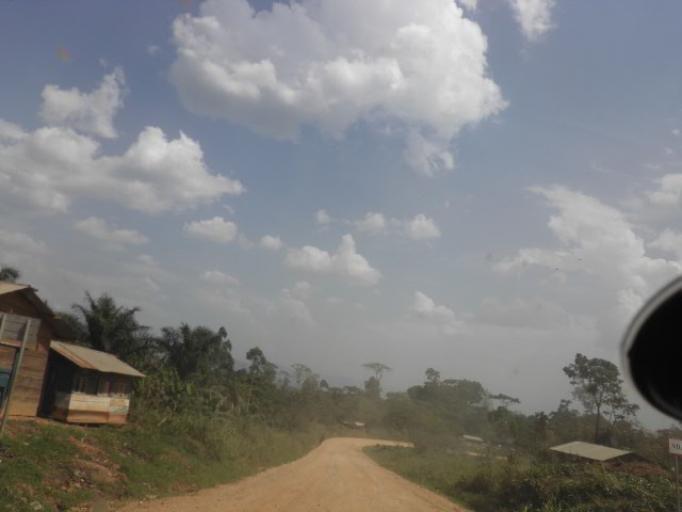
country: CD
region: Nord Kivu
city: Beni
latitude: 1.0156
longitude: 29.5873
